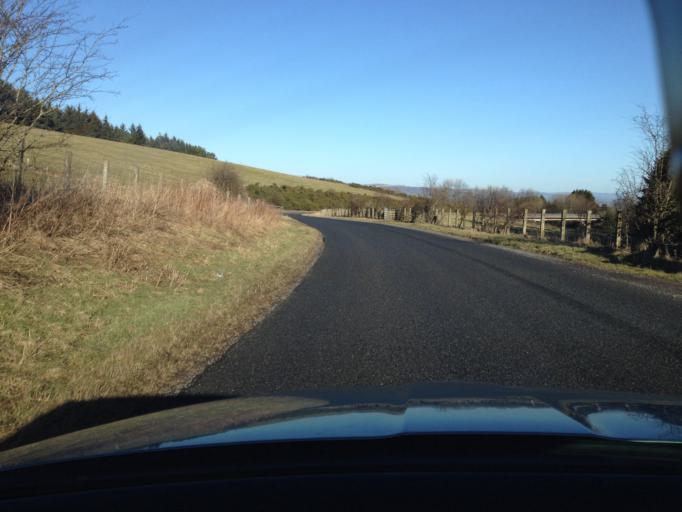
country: GB
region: Scotland
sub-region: Perth and Kinross
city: Bridge of Earn
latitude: 56.3137
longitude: -3.3744
